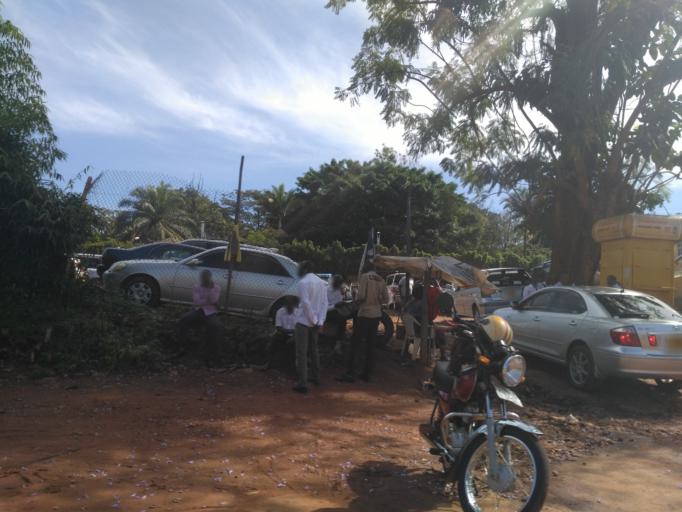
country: UG
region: Central Region
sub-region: Kampala District
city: Kampala
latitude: 0.3178
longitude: 32.5785
